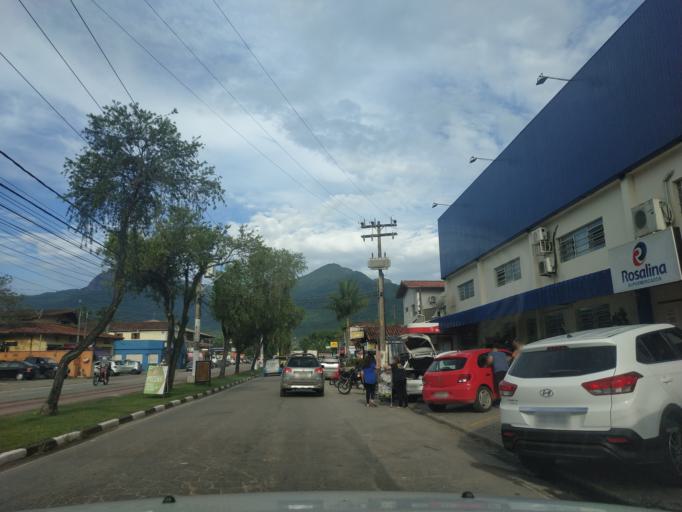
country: BR
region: Sao Paulo
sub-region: Ilhabela
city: Ilhabela
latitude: -23.8221
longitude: -45.3744
